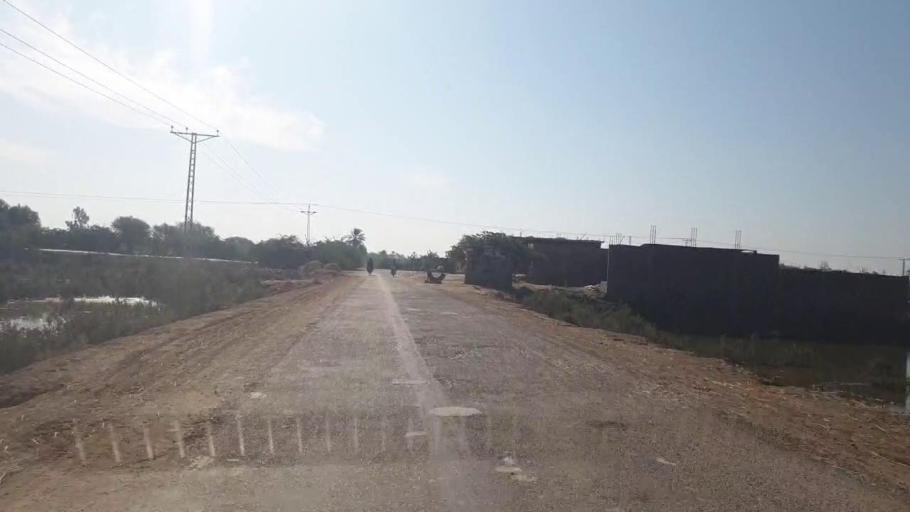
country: PK
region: Sindh
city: Talhar
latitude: 24.8979
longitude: 68.8254
